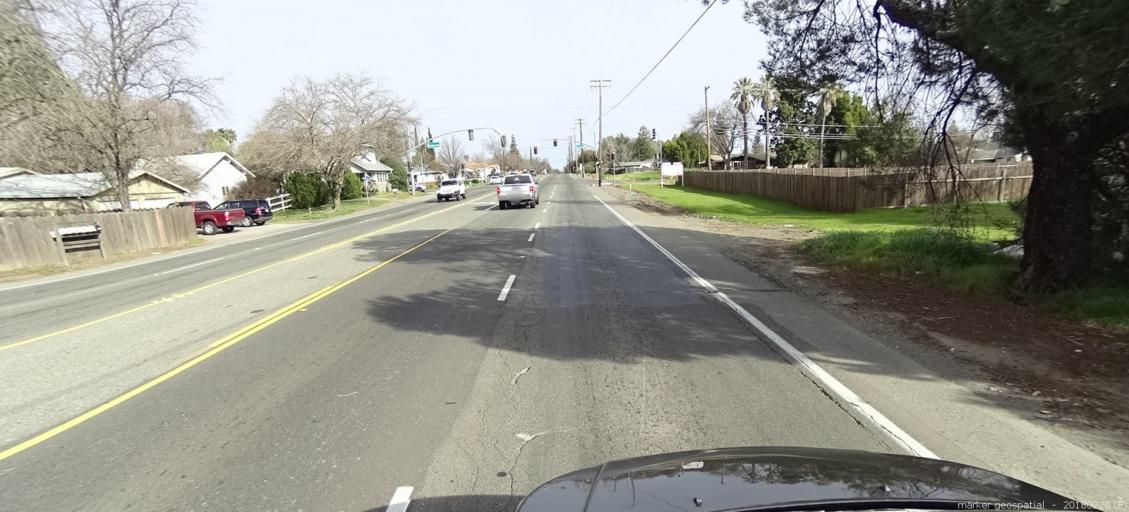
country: US
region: California
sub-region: Sacramento County
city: Orangevale
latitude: 38.6850
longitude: -121.2255
